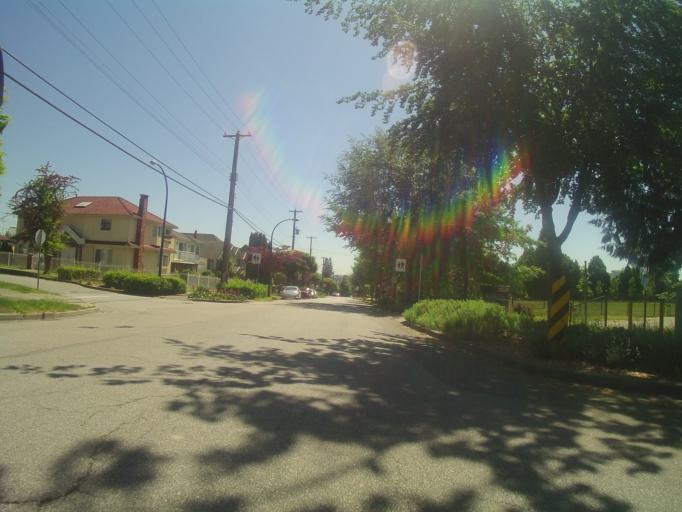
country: CA
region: British Columbia
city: Vancouver
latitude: 49.2179
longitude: -123.1063
